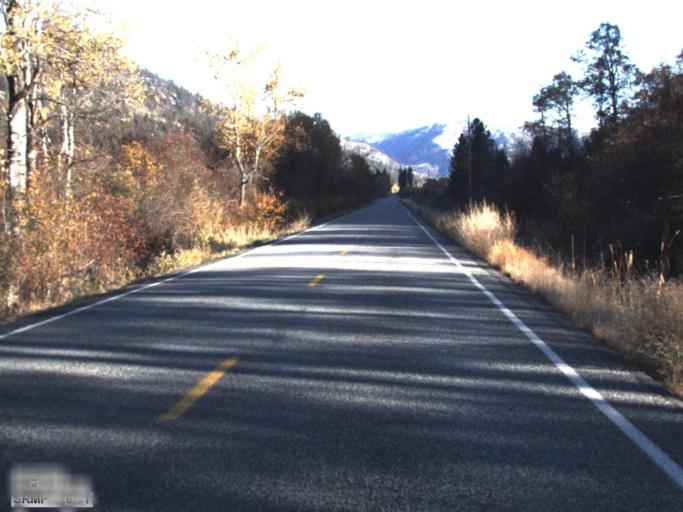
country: US
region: Washington
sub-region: Okanogan County
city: Coulee Dam
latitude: 48.2097
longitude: -118.7114
